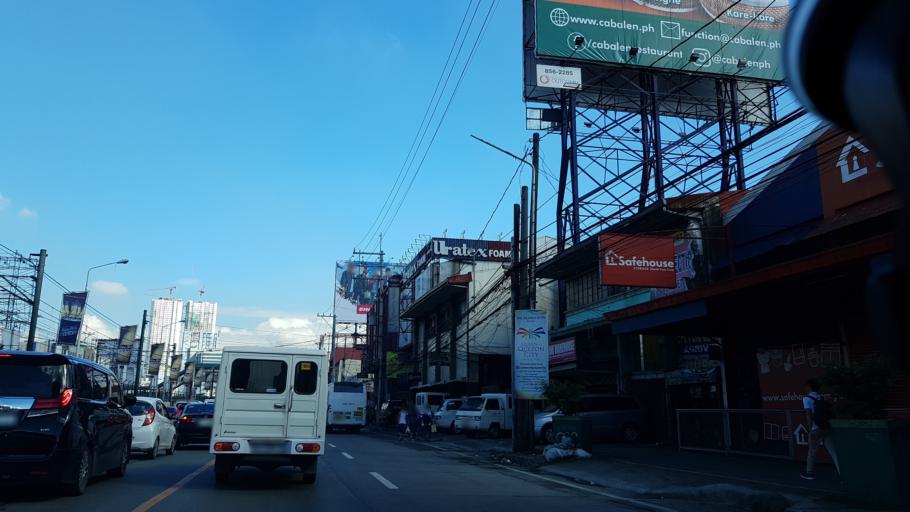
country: PH
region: Metro Manila
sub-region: Quezon City
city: Quezon City
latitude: 14.6261
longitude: 121.0482
